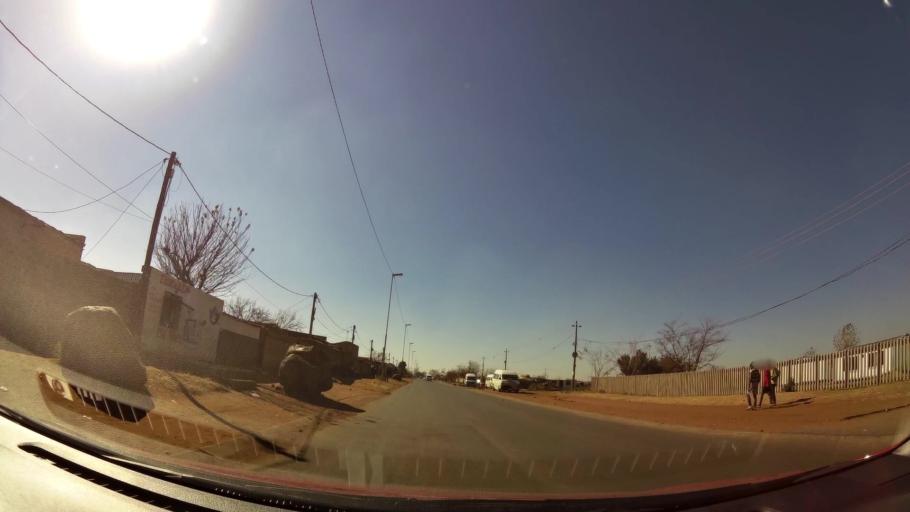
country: ZA
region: Gauteng
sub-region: City of Johannesburg Metropolitan Municipality
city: Soweto
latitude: -26.2242
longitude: 27.8294
